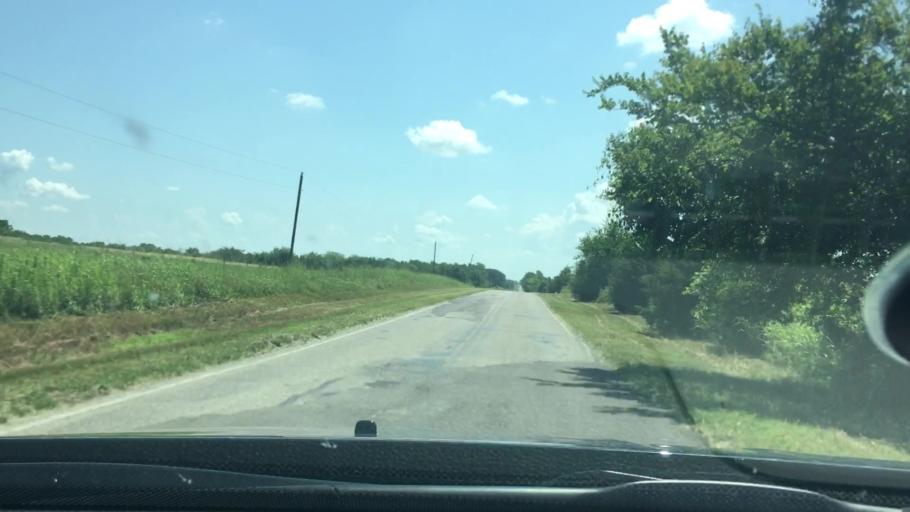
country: US
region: Oklahoma
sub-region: Pontotoc County
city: Ada
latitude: 34.6945
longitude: -96.5634
